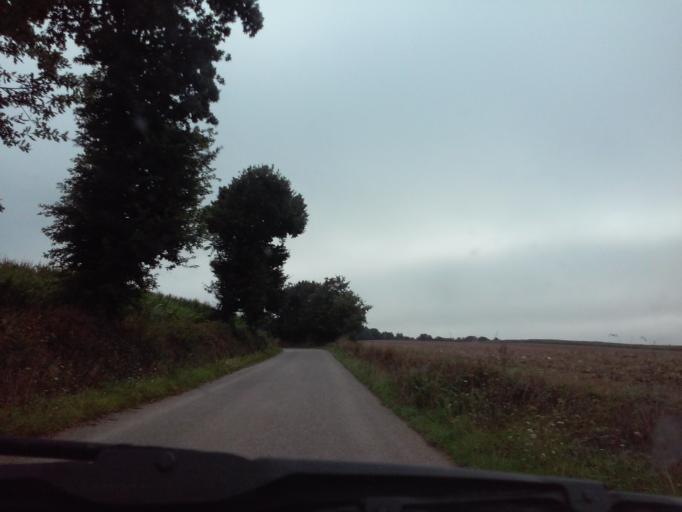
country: FR
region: Brittany
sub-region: Departement du Morbihan
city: Taupont
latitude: 48.0098
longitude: -2.4503
